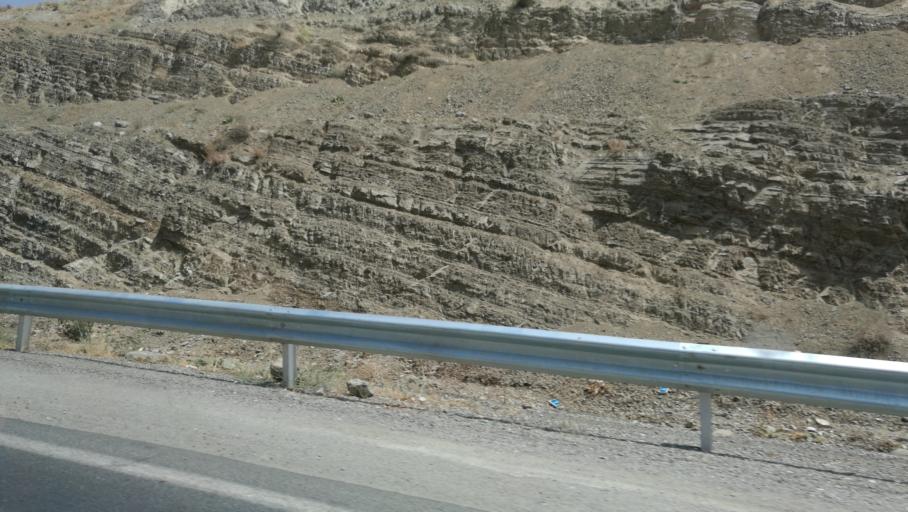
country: IR
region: Alborz
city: Karaj
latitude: 35.8241
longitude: 51.0401
